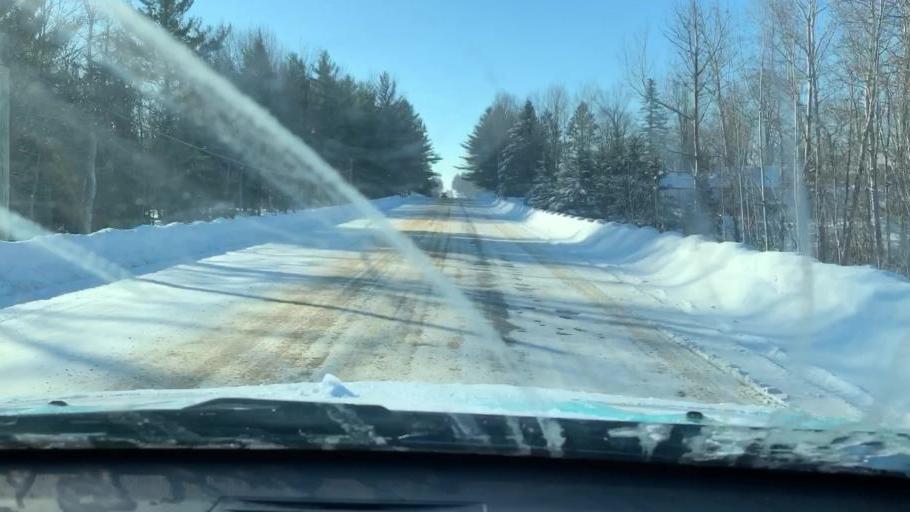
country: US
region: Michigan
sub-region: Osceola County
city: Evart
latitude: 44.0990
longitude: -85.2464
